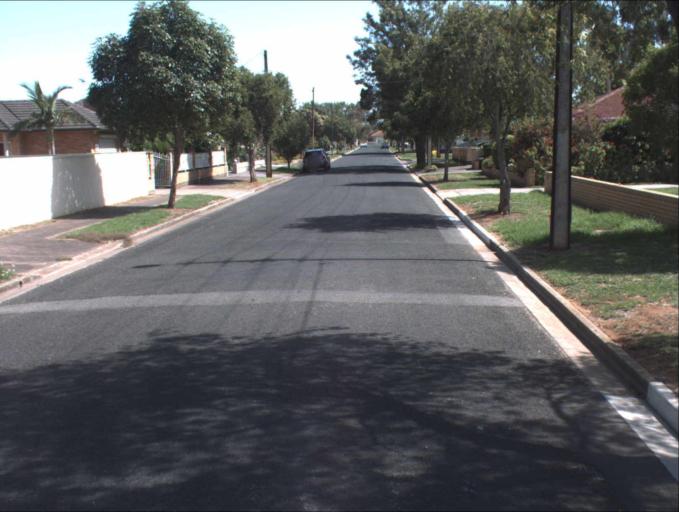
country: AU
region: South Australia
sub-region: Port Adelaide Enfield
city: Klemzig
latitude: -34.8821
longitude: 138.6440
